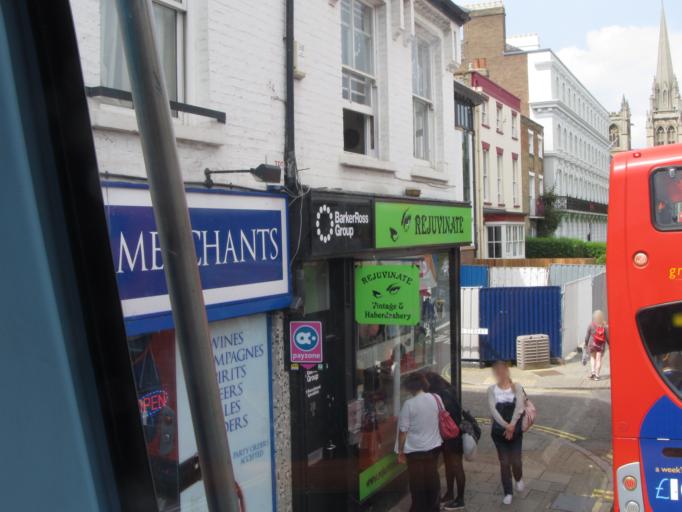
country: GB
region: England
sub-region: Cambridgeshire
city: Cambridge
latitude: 52.1974
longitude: 0.1291
